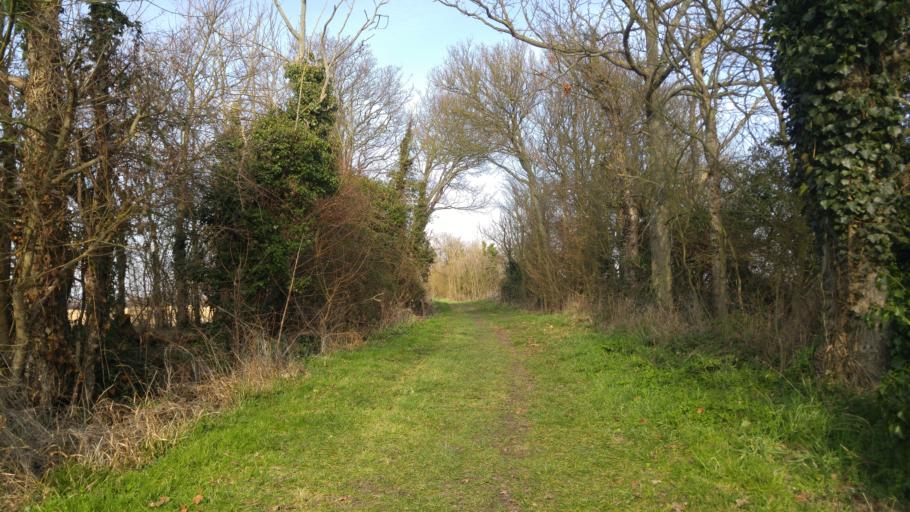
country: GB
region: England
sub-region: Essex
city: Little Clacton
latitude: 51.8201
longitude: 1.1707
